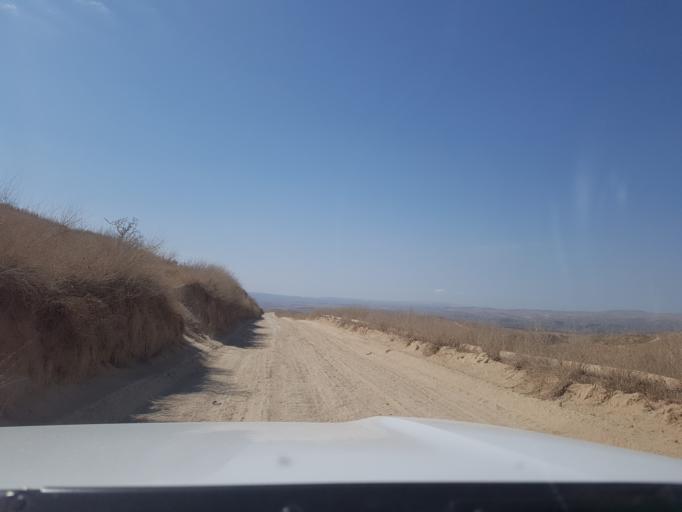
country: TM
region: Ahal
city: Baharly
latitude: 38.2700
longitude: 56.8944
